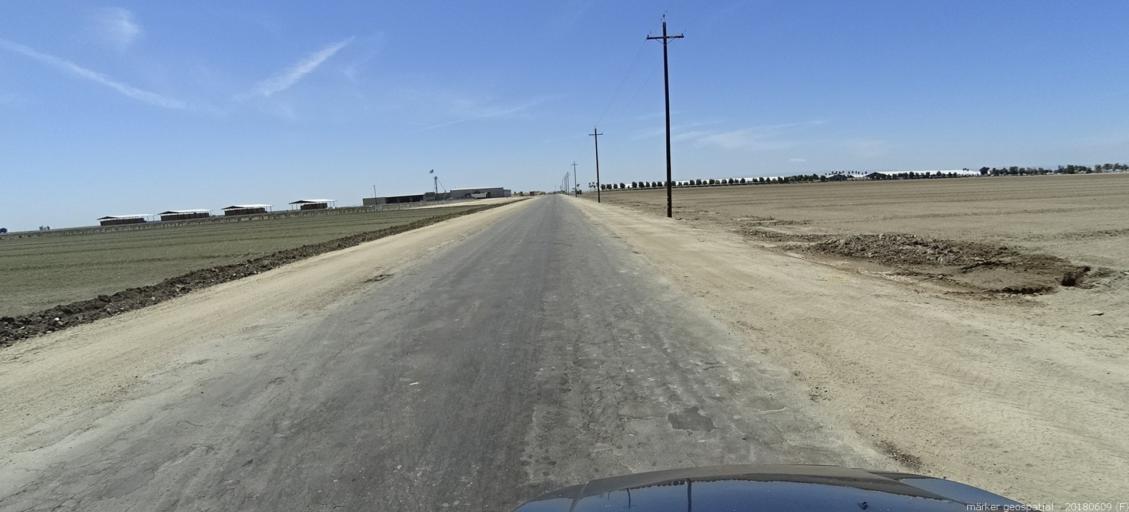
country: US
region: California
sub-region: Madera County
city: Fairmead
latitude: 36.9452
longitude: -120.2917
